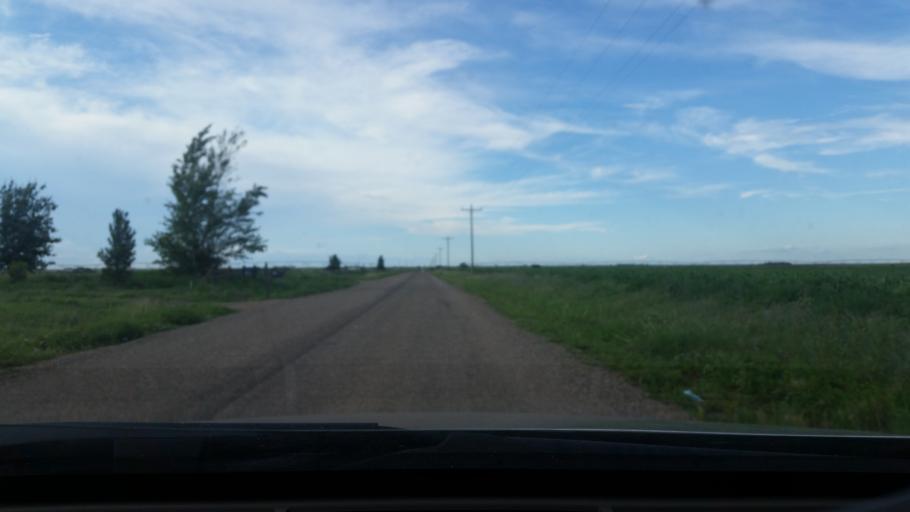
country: US
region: New Mexico
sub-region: Curry County
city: Clovis
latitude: 34.4638
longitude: -103.1789
